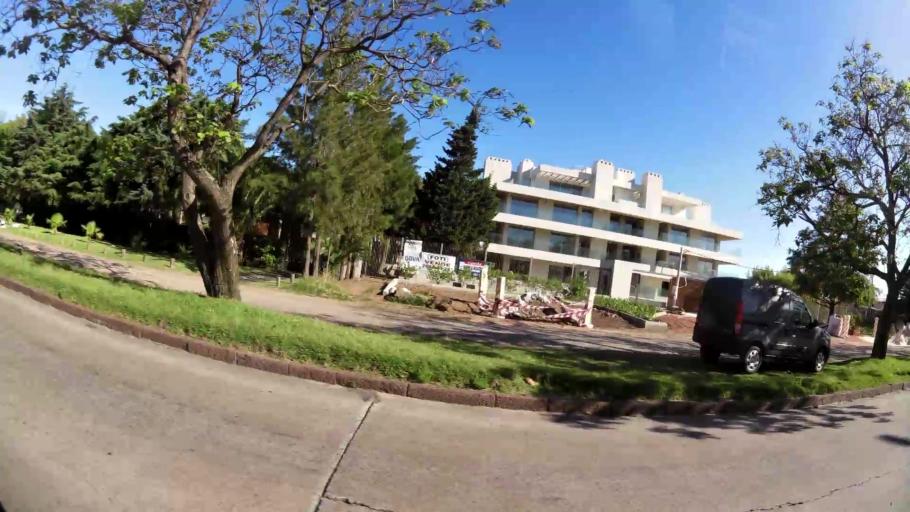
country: UY
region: Canelones
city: Paso de Carrasco
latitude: -34.8786
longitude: -56.0705
